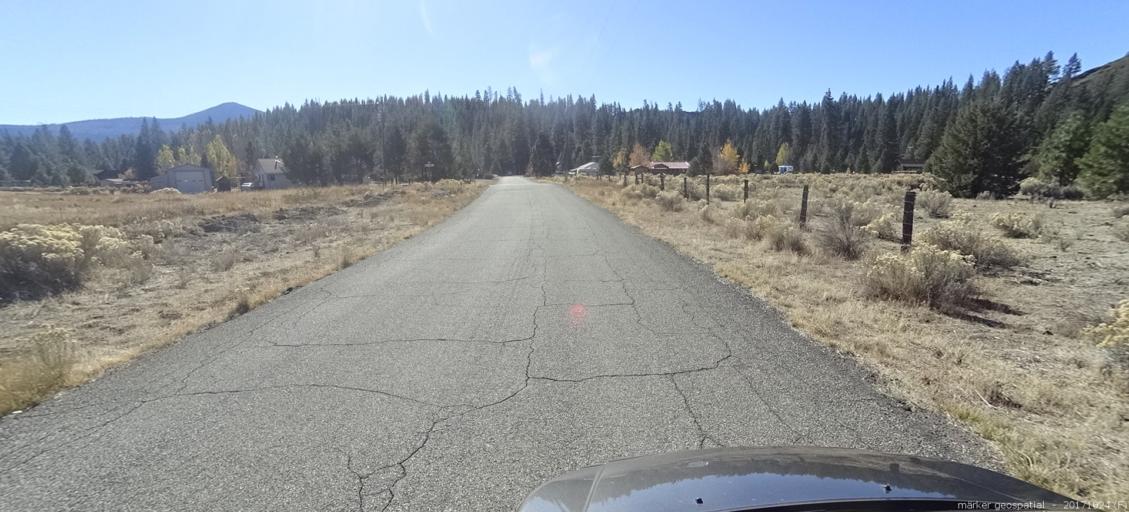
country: US
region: California
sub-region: Shasta County
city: Burney
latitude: 40.6743
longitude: -121.4306
